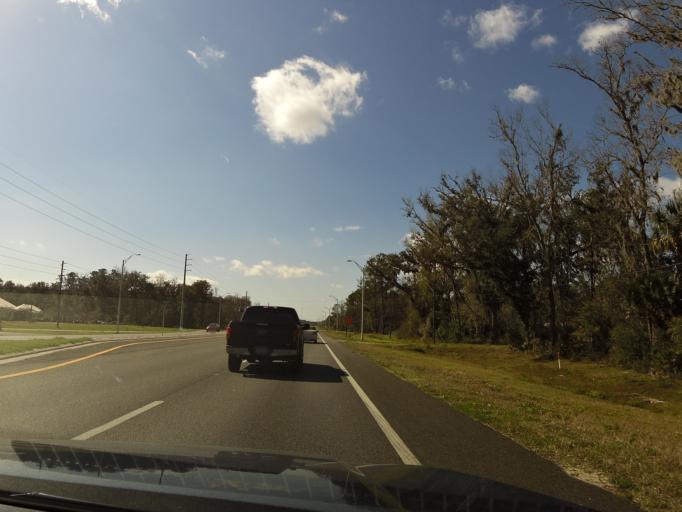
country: US
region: Florida
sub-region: Putnam County
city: East Palatka
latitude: 29.5943
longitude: -81.6002
